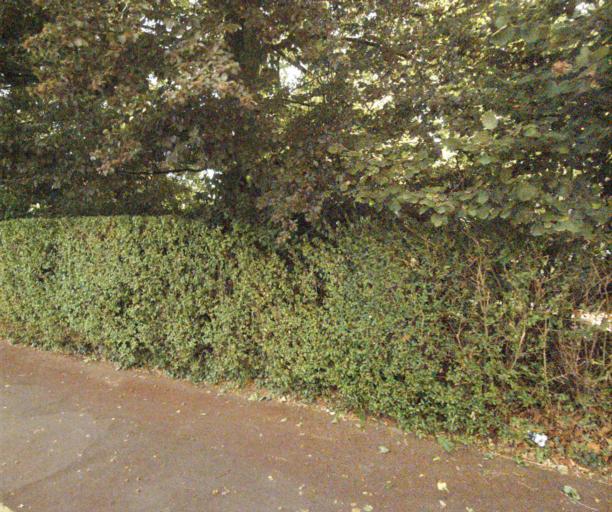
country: FR
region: Nord-Pas-de-Calais
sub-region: Departement du Nord
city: Linselles
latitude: 50.7370
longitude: 3.0722
